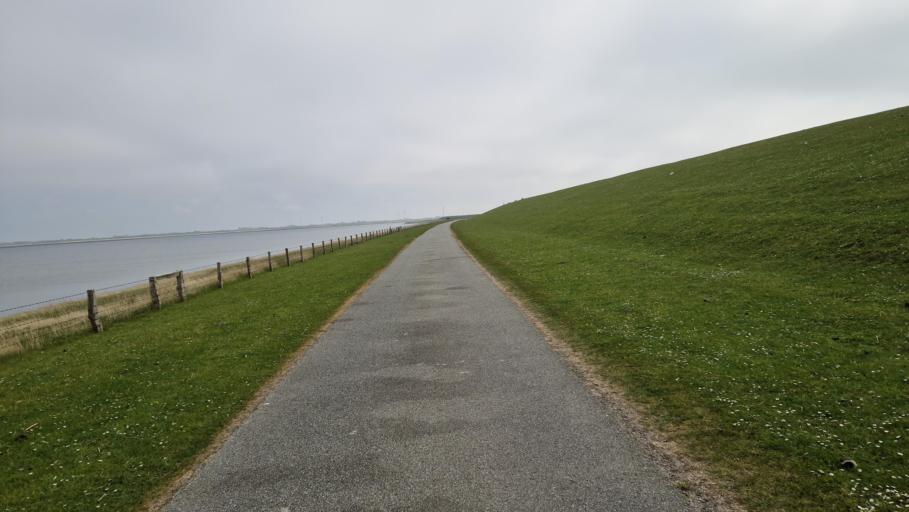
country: DE
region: Schleswig-Holstein
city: Elisabeth-Sophien-Koog
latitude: 54.5473
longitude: 8.8789
